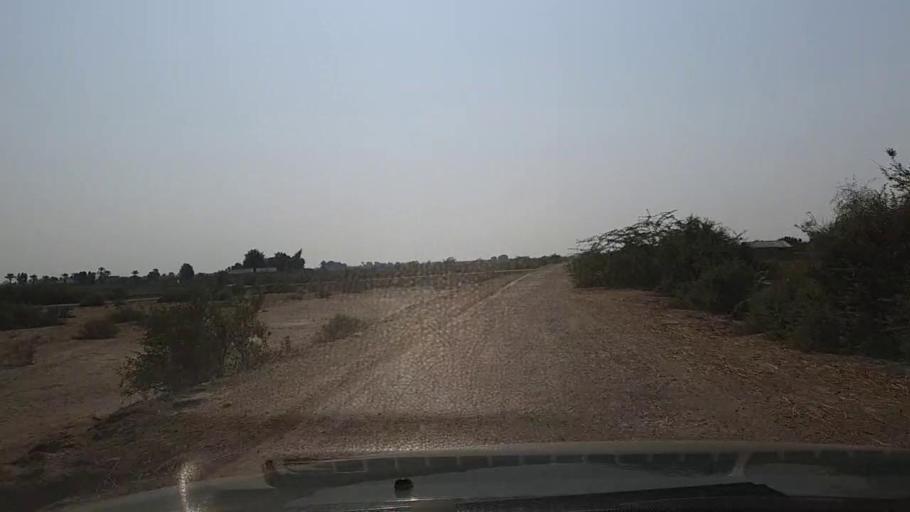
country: PK
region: Sindh
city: Mirpur Sakro
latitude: 24.3835
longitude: 67.6622
